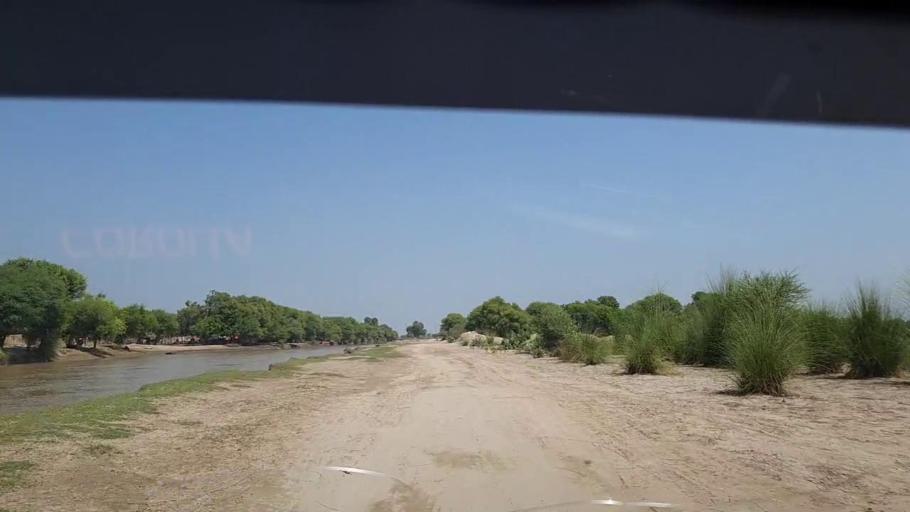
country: PK
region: Sindh
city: Tangwani
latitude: 28.2340
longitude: 68.9791
